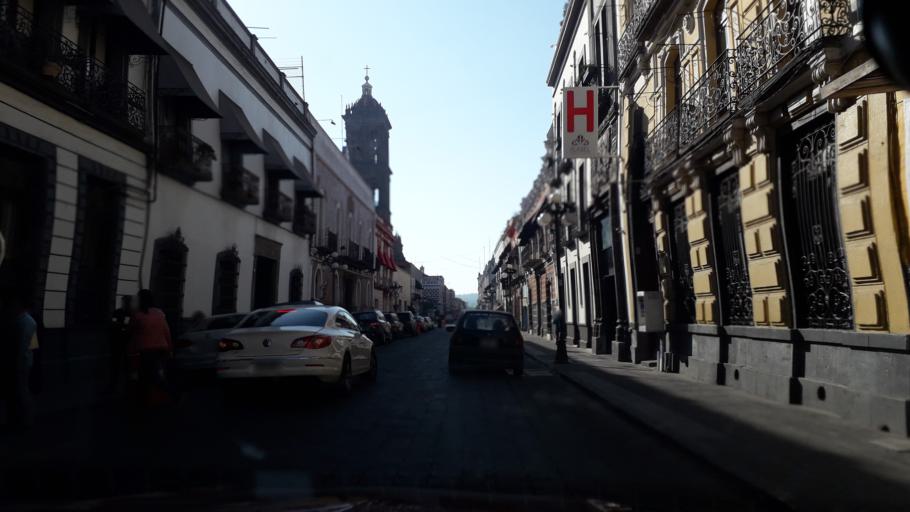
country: MX
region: Puebla
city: Puebla
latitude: 19.0435
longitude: -98.2006
